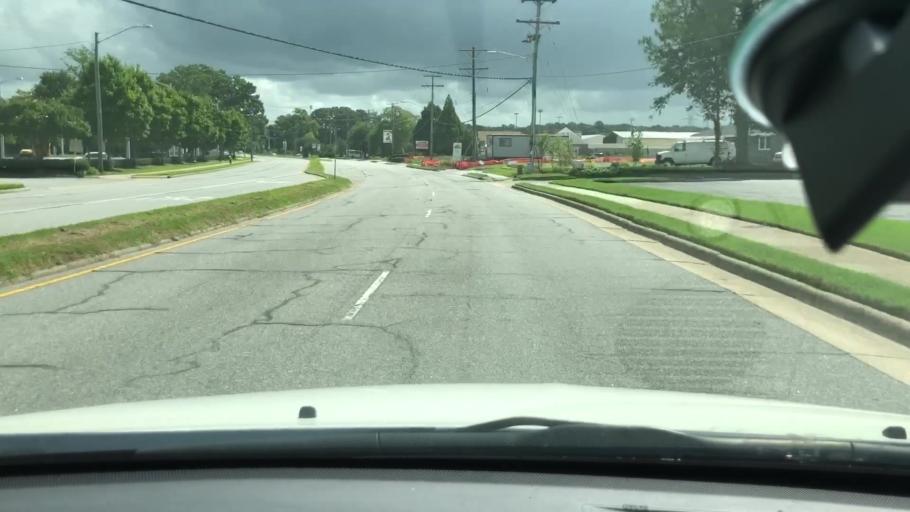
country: US
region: Virginia
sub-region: City of Chesapeake
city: Chesapeake
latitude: 36.8127
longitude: -76.2026
